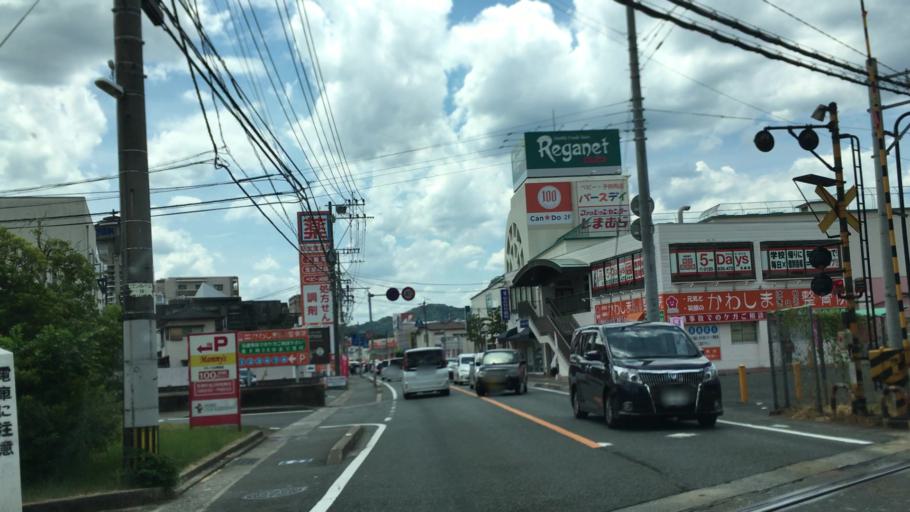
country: JP
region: Fukuoka
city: Dazaifu
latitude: 33.5106
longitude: 130.5250
